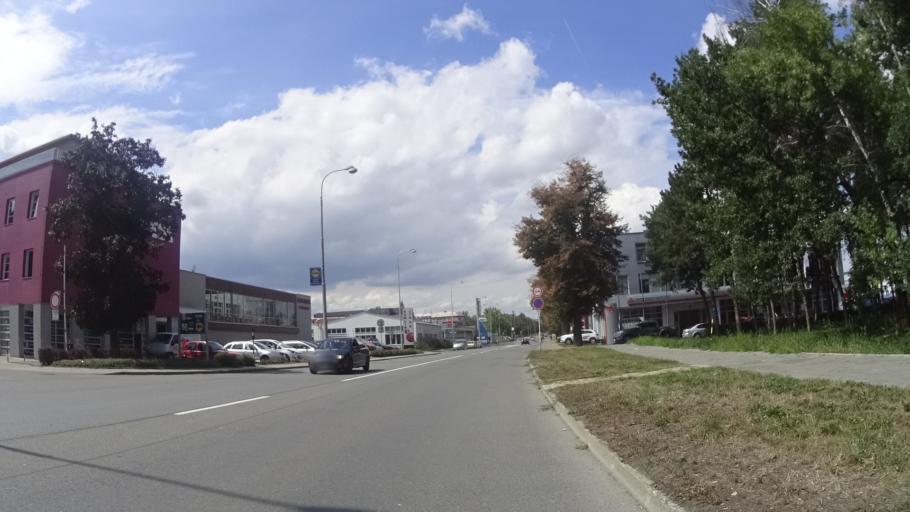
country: CZ
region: Olomoucky
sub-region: Okres Olomouc
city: Olomouc
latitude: 49.6017
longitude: 17.2456
